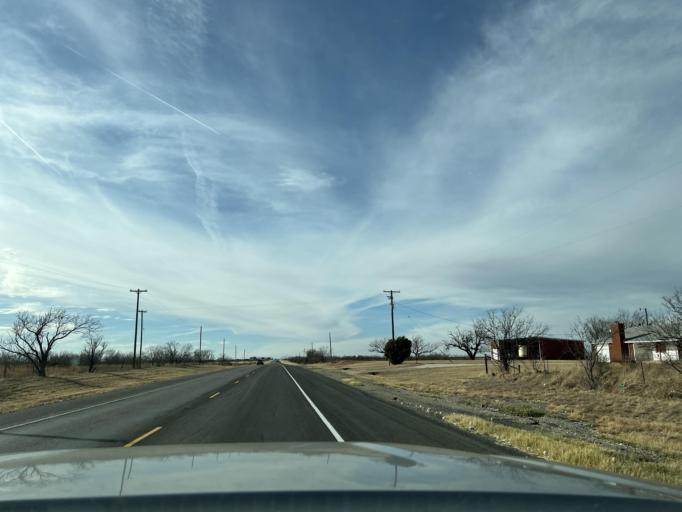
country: US
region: Texas
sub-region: Jones County
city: Anson
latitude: 32.7517
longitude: -99.9288
